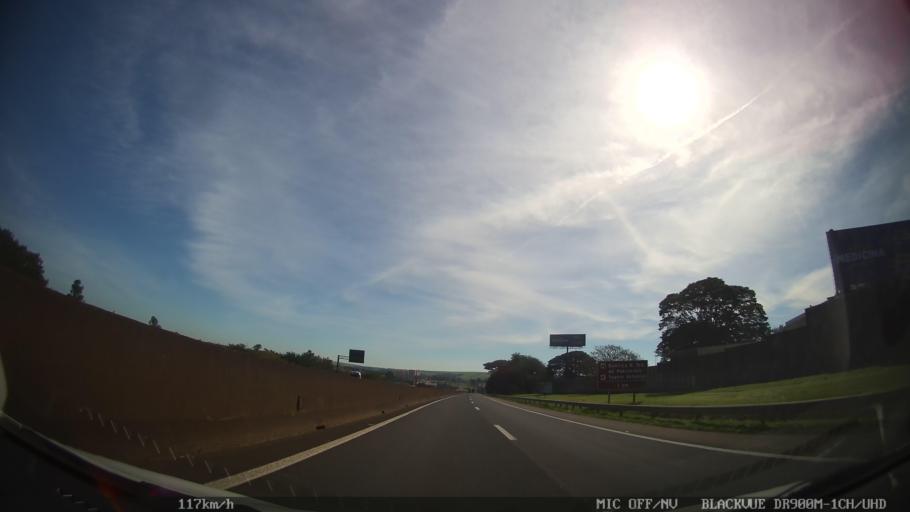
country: BR
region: Sao Paulo
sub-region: Araras
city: Araras
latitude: -22.3709
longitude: -47.3946
